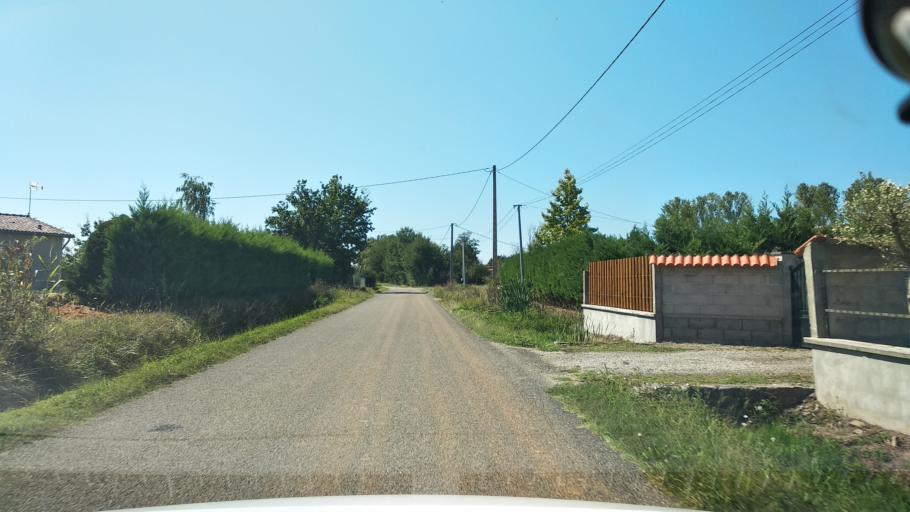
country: FR
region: Midi-Pyrenees
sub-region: Departement du Tarn-et-Garonne
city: Saint-Porquier
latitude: 44.0352
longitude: 1.2312
